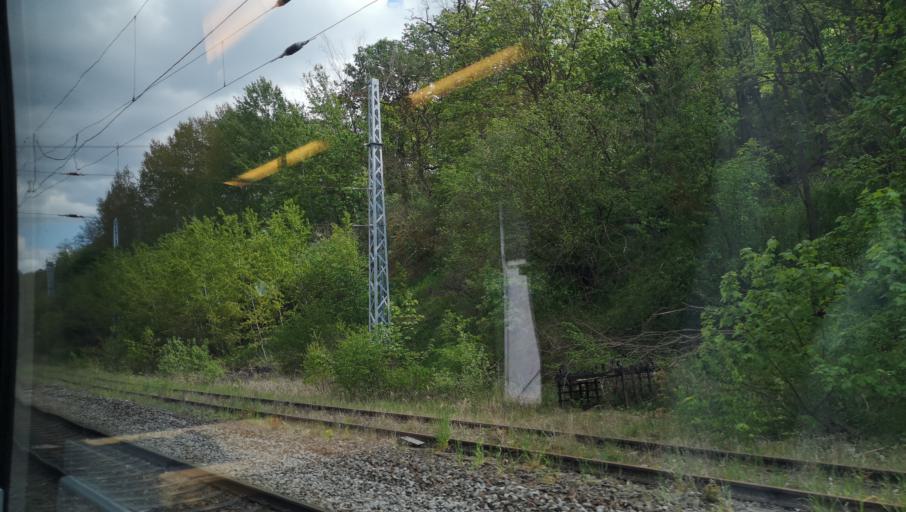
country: DE
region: Saxony-Anhalt
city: Blankenheim
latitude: 51.5111
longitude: 11.4435
